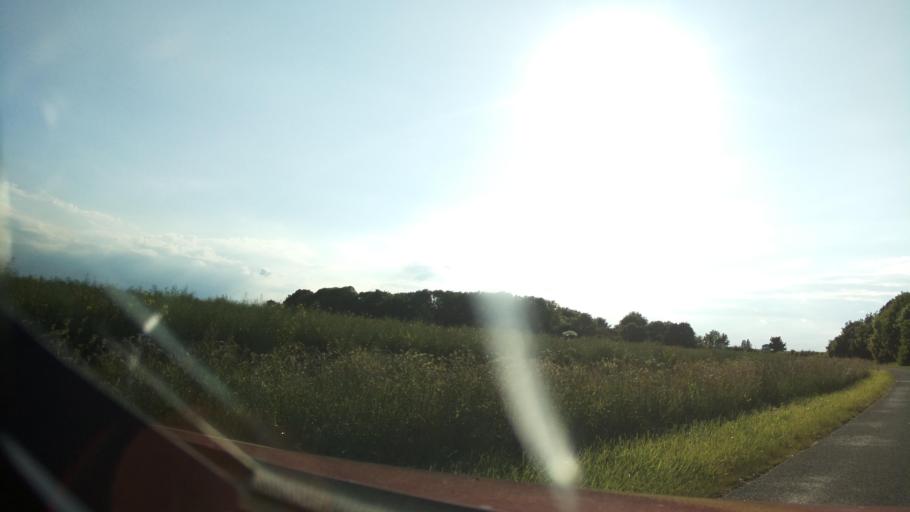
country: GB
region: England
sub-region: Lincolnshire
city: Navenby
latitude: 53.1129
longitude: -0.5991
